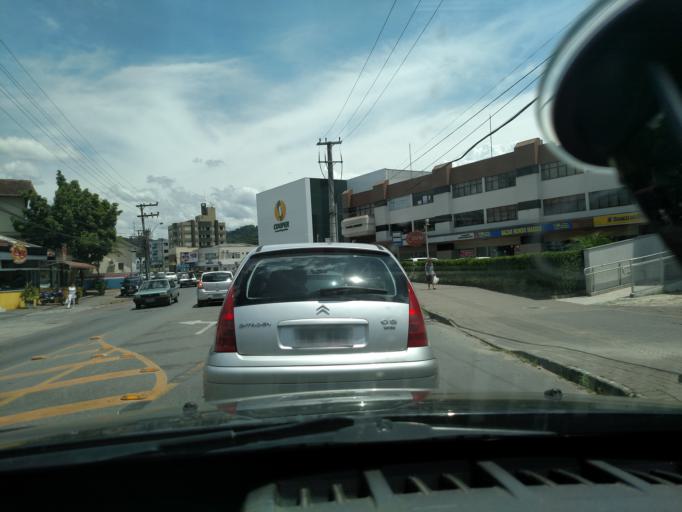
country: BR
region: Santa Catarina
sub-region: Blumenau
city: Blumenau
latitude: -26.9439
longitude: -49.0717
